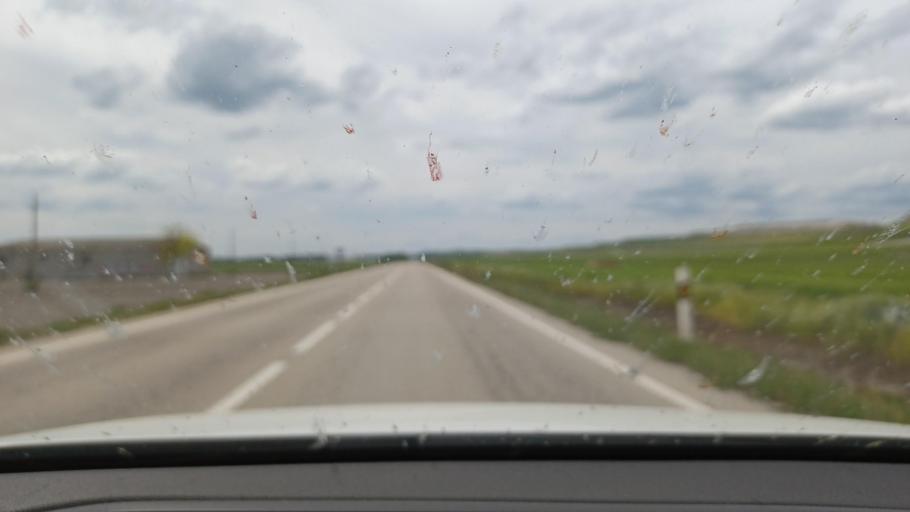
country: ES
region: Castille and Leon
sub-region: Provincia de Segovia
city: Frumales
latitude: 41.3842
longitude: -4.2458
